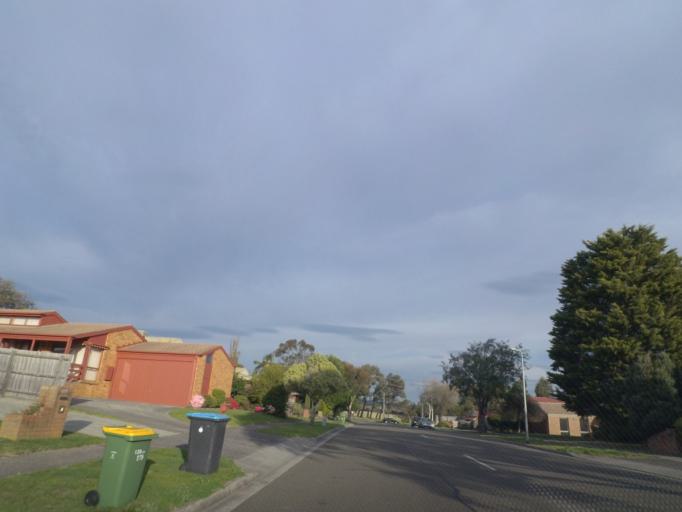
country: AU
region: Victoria
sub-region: Knox
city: Ferntree Gully
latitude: -37.9087
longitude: 145.2756
